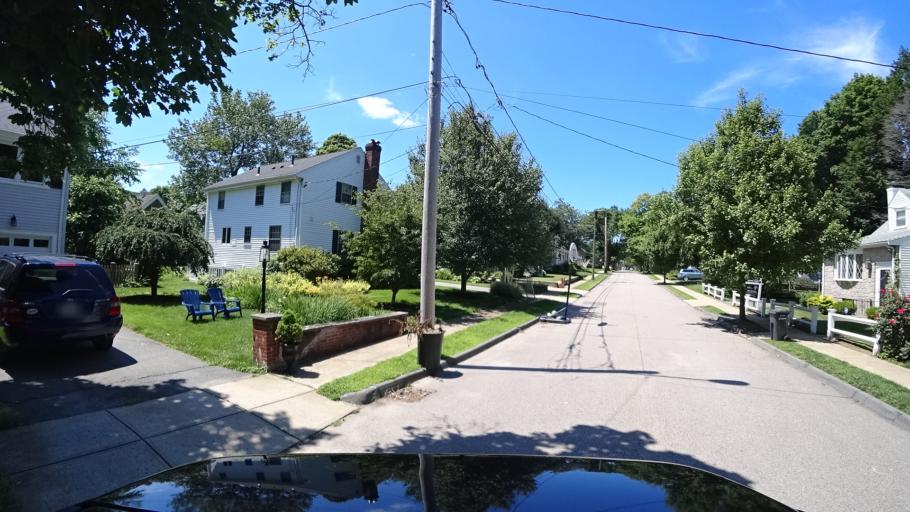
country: US
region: Massachusetts
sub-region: Norfolk County
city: Dedham
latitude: 42.2384
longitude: -71.1566
